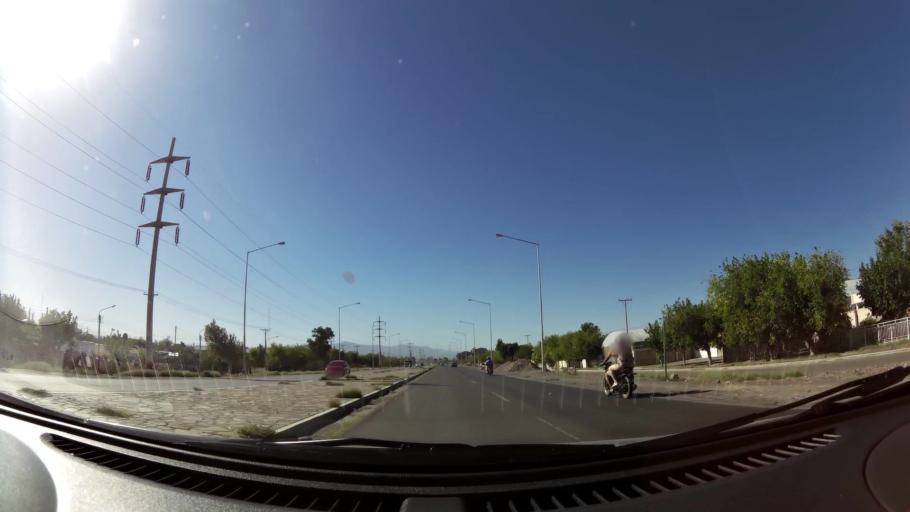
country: AR
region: San Juan
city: Villa Paula de Sarmiento
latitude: -31.5062
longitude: -68.5176
